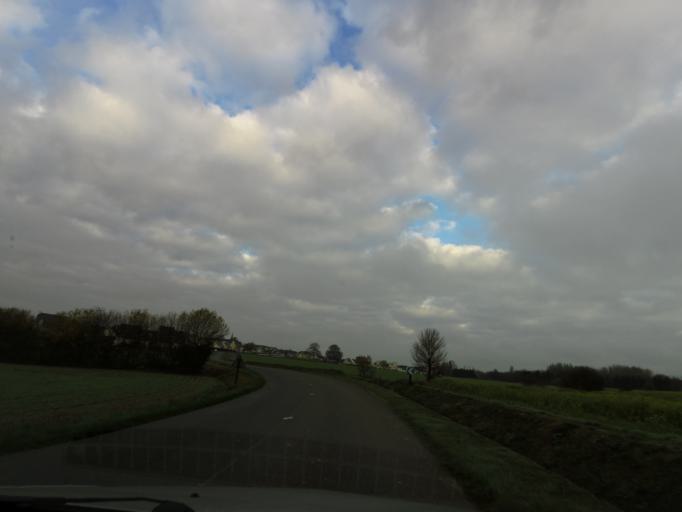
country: FR
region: Brittany
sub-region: Departement d'Ille-et-Vilaine
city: Orgeres
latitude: 47.9916
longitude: -1.6619
